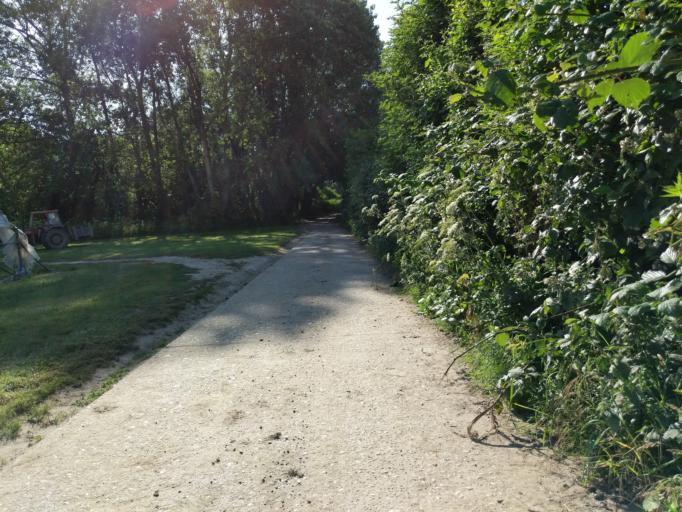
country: GB
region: England
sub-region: Kent
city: Faversham
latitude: 51.3300
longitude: 0.9291
